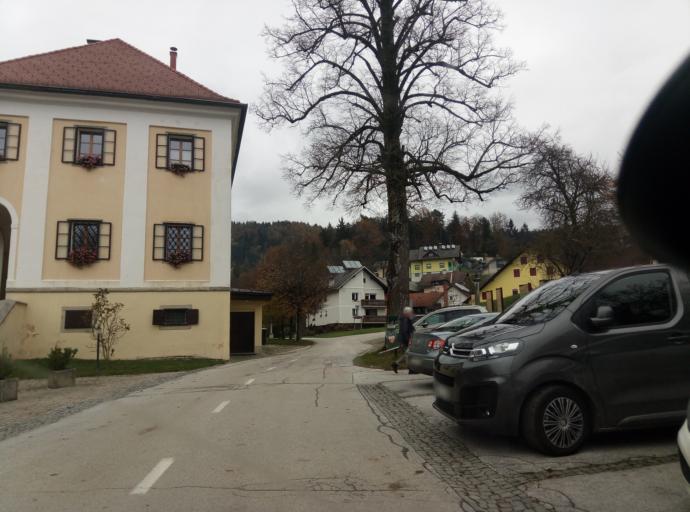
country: SI
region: Cerklje na Gorenjskem
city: Cerklje na Gorenjskem
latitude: 46.2711
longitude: 14.4650
